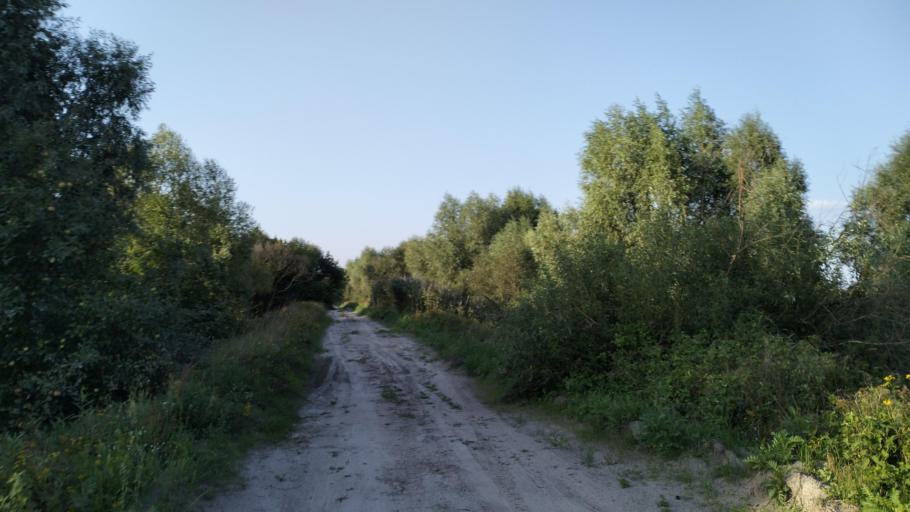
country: BY
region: Brest
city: Davyd-Haradok
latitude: 52.0280
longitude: 27.1946
